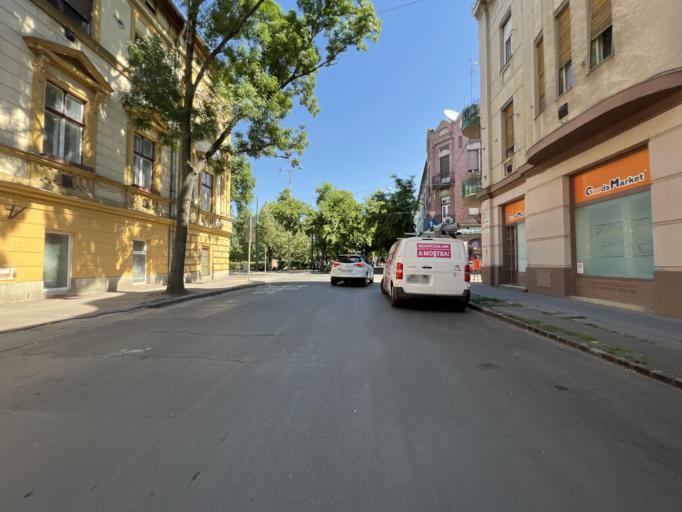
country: HU
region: Csongrad
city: Szeged
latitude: 46.2542
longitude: 20.1441
